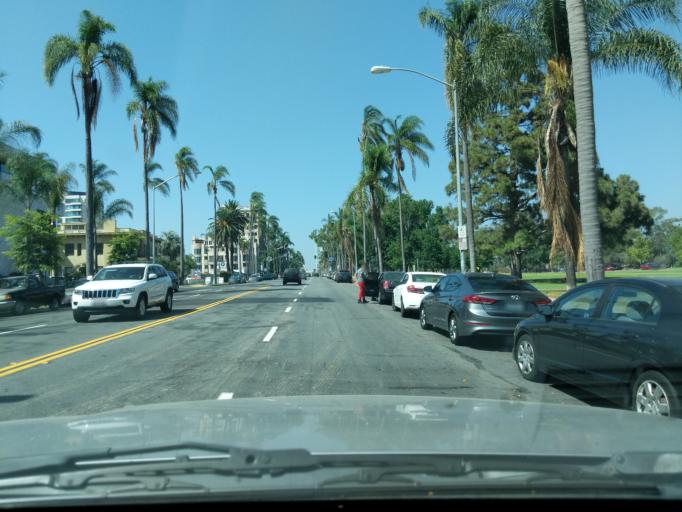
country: US
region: California
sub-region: San Diego County
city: San Diego
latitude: 32.7350
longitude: -117.1594
